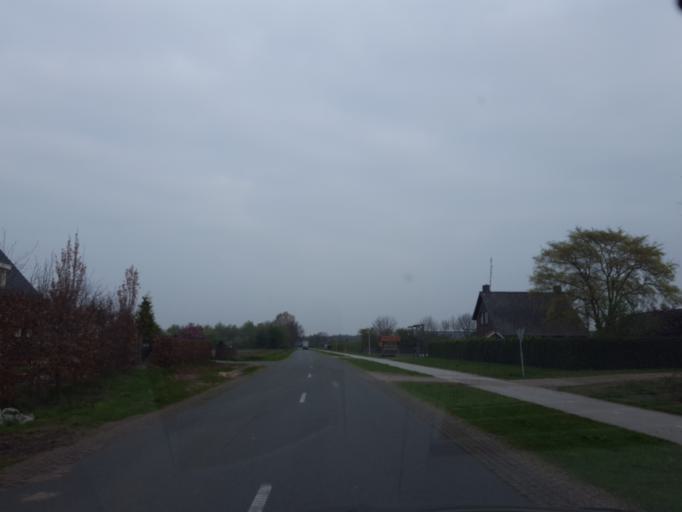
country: NL
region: North Brabant
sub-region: Gemeente Someren
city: Someren
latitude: 51.3240
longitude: 5.6976
